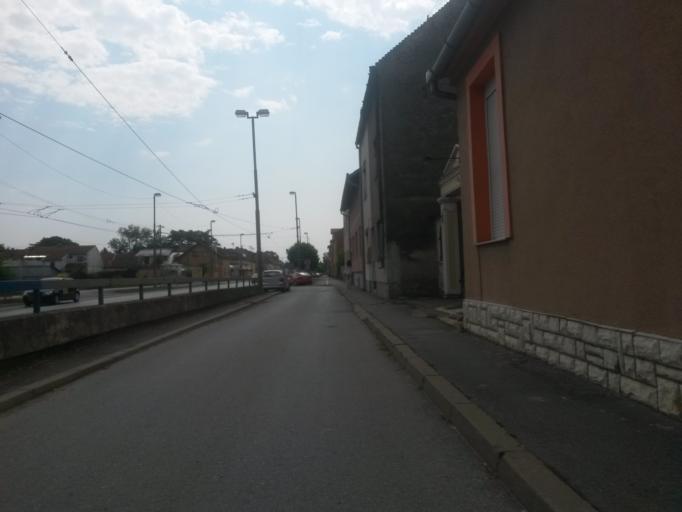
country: HR
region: Osjecko-Baranjska
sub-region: Grad Osijek
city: Osijek
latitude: 45.5512
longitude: 18.6774
